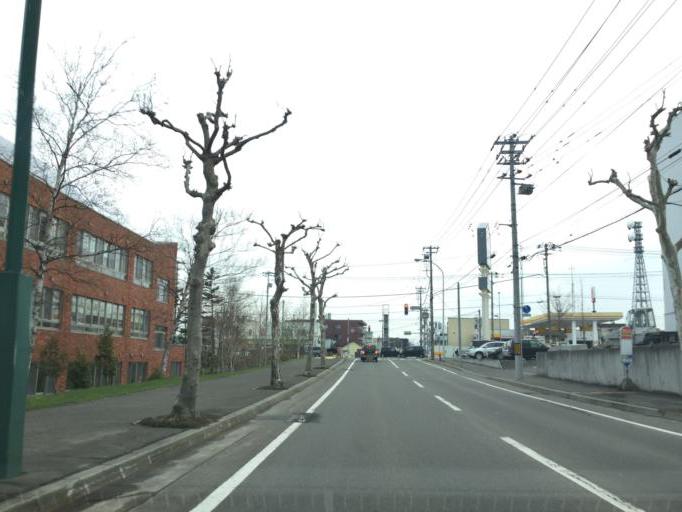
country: JP
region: Hokkaido
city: Iwamizawa
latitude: 43.2100
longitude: 141.7837
